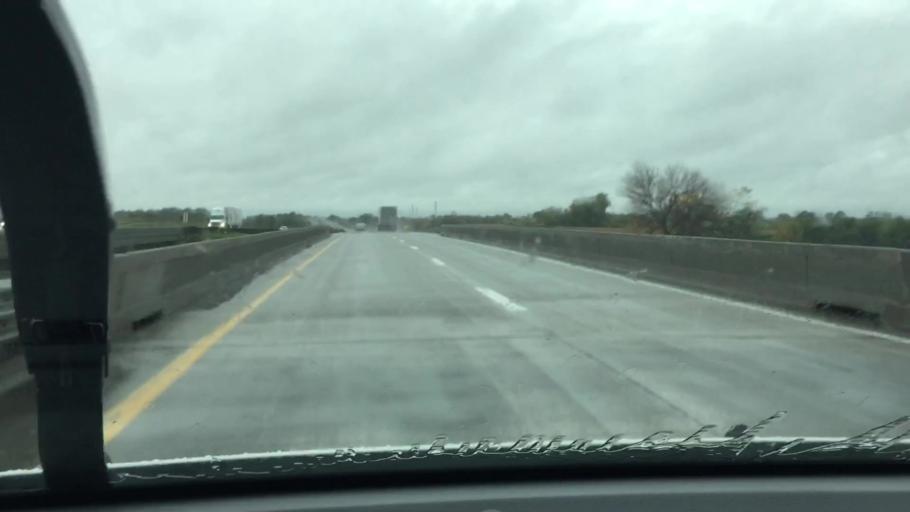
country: US
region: Iowa
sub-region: Poweshiek County
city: Brooklyn
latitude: 41.6966
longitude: -92.5520
